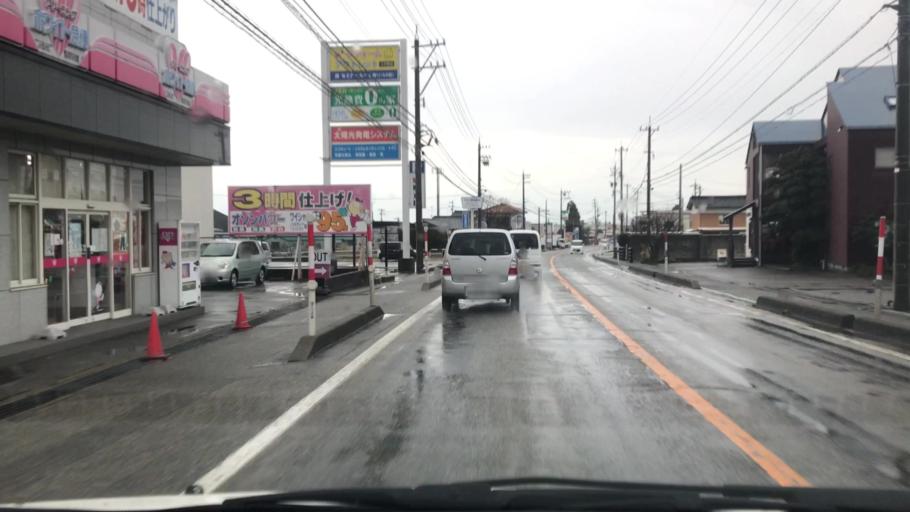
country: JP
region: Toyama
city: Yatsuomachi-higashikumisaka
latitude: 36.6028
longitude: 137.2033
